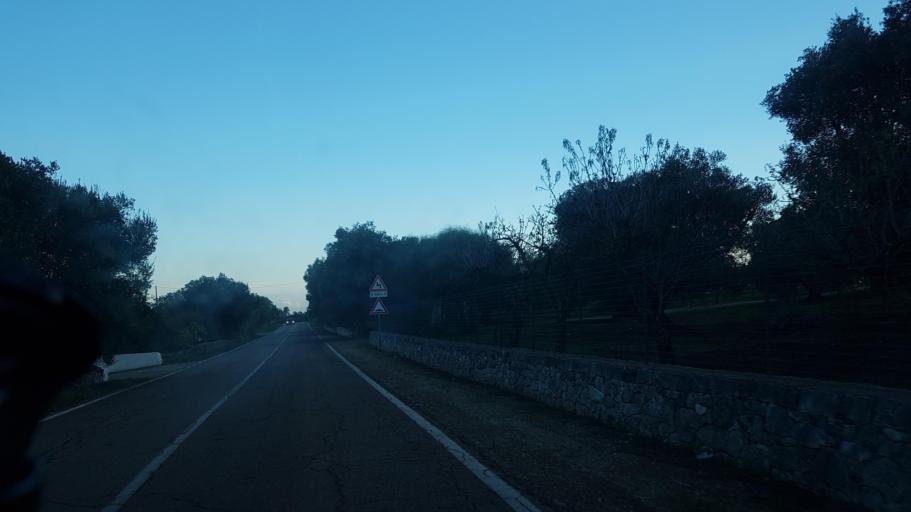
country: IT
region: Apulia
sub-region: Provincia di Brindisi
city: Ostuni
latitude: 40.6930
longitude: 17.5969
